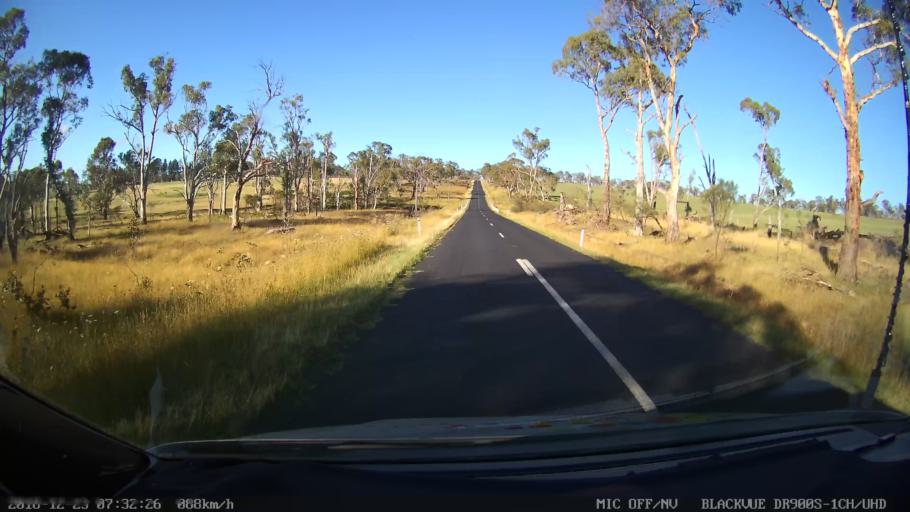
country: AU
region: New South Wales
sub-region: Armidale Dumaresq
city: Enmore
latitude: -30.5047
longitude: 152.1170
